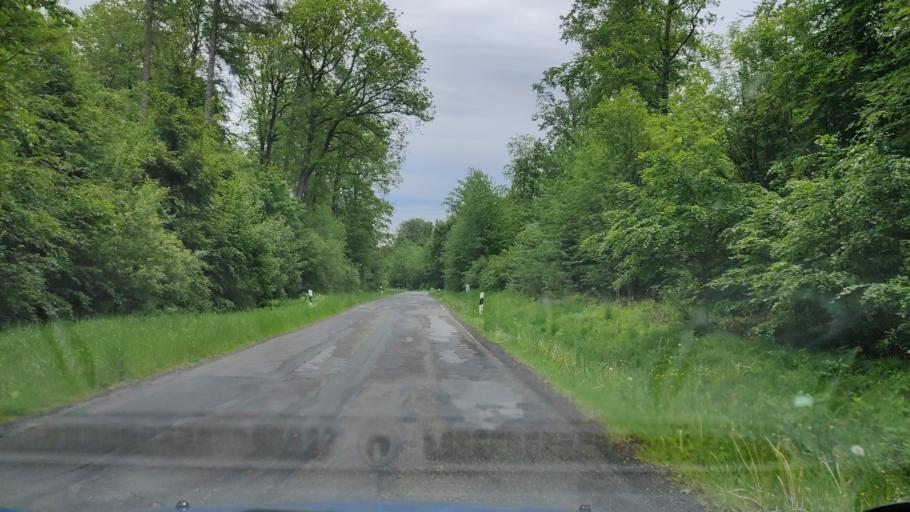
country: DE
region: Lower Saxony
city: Hardegsen
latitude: 51.7088
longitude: 9.7682
